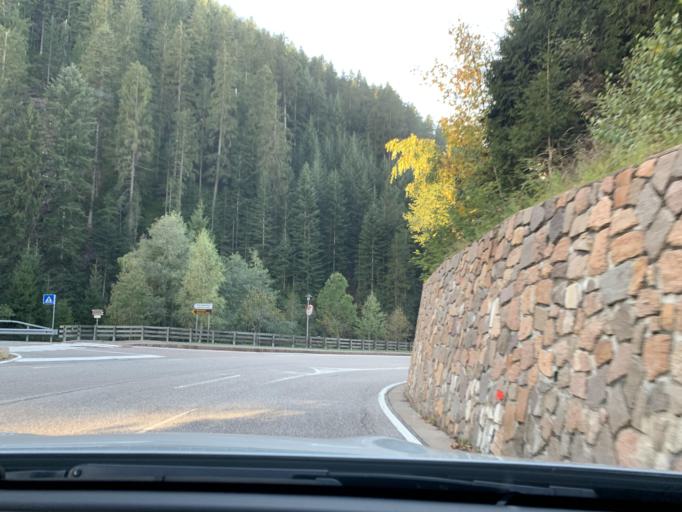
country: IT
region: Trentino-Alto Adige
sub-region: Bolzano
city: Nova Levante
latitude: 46.4276
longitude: 11.5385
